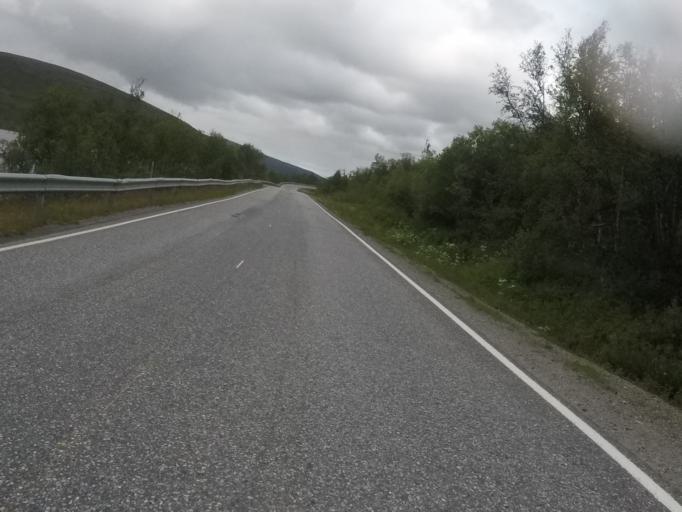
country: NO
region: Finnmark Fylke
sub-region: Alta
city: Alta
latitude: 69.6741
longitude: 23.4323
